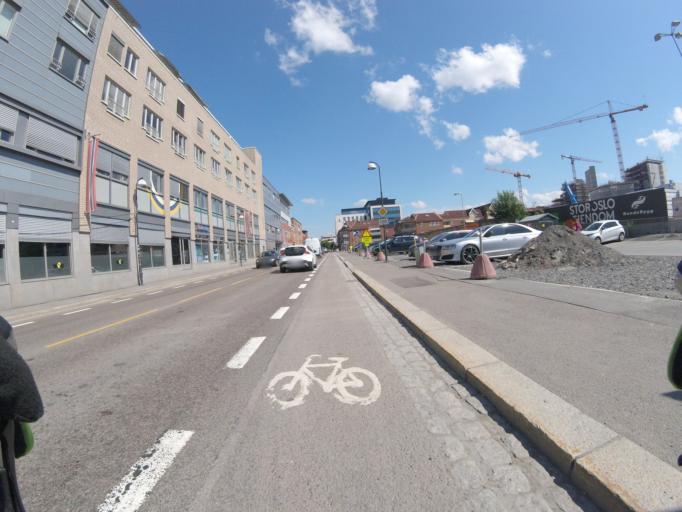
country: NO
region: Akershus
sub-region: Skedsmo
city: Lillestrom
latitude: 59.9555
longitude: 11.0500
